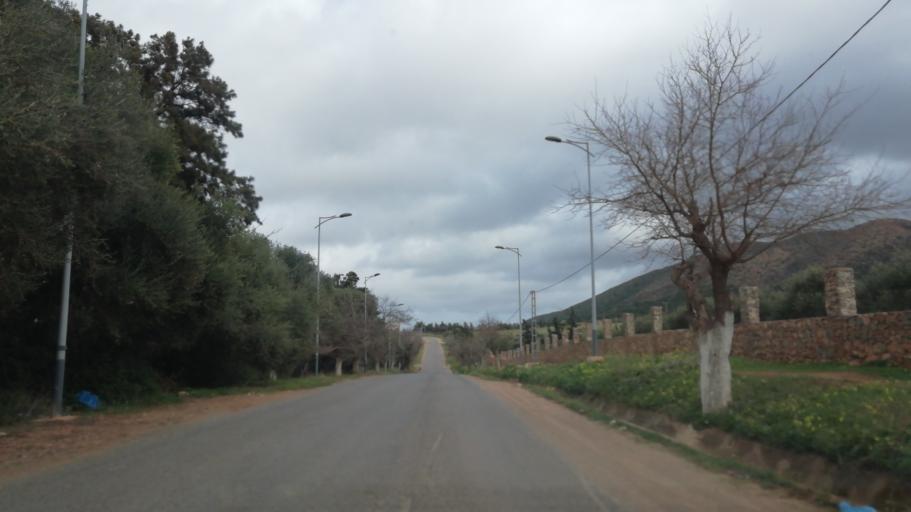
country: DZ
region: Oran
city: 'Ain el Turk
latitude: 35.6891
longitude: -0.8649
